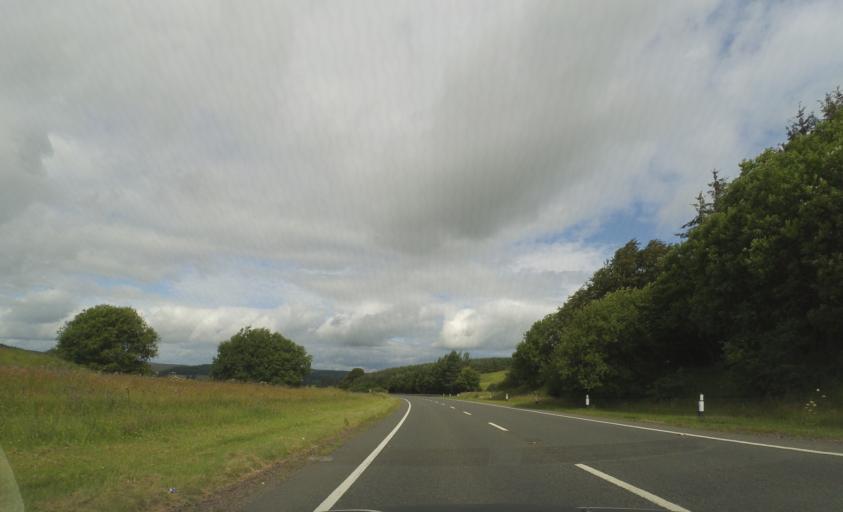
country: GB
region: Scotland
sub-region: The Scottish Borders
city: Hawick
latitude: 55.4792
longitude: -2.8193
